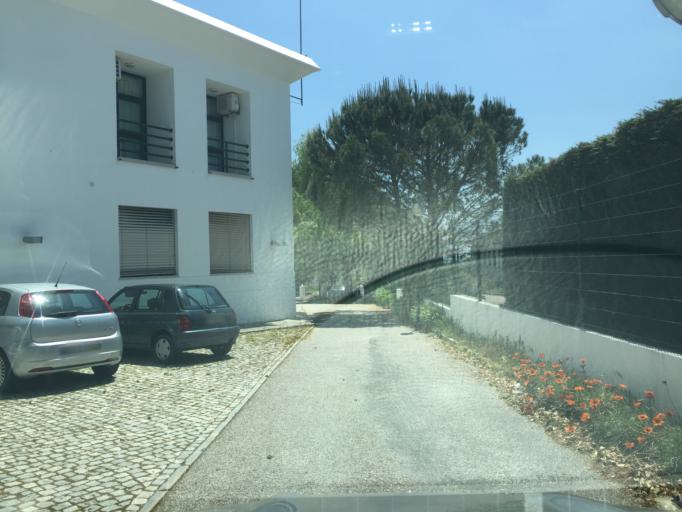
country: PT
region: Castelo Branco
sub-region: Vila de Rei
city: Vila de Rei
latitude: 39.6766
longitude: -8.1433
